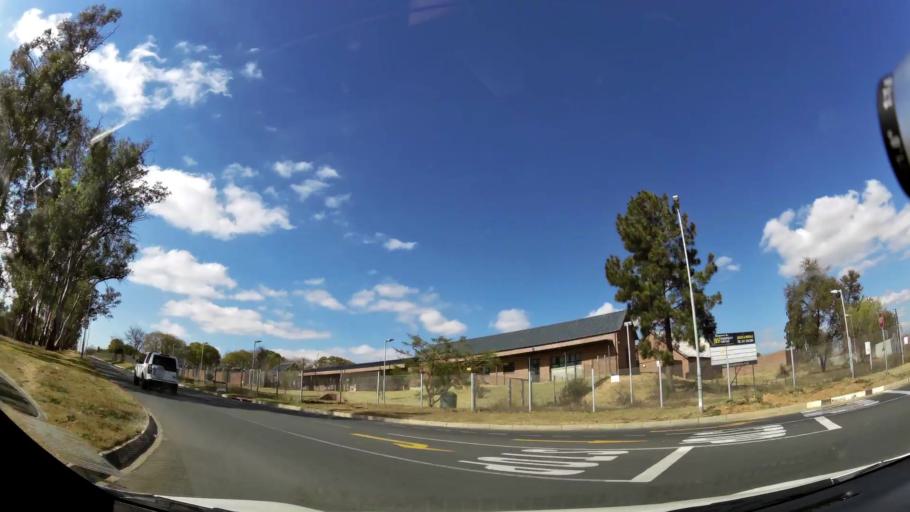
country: ZA
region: Gauteng
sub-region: City of Johannesburg Metropolitan Municipality
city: Midrand
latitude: -25.9965
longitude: 28.0942
